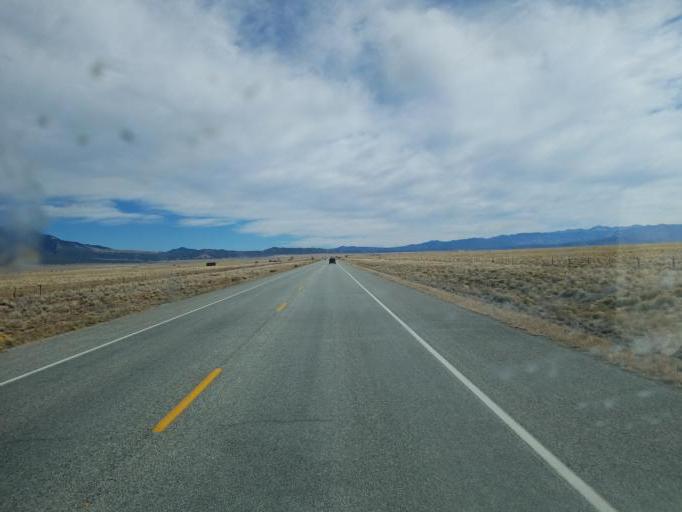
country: US
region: Colorado
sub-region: Alamosa County
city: Alamosa East
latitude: 37.4750
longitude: -105.6143
